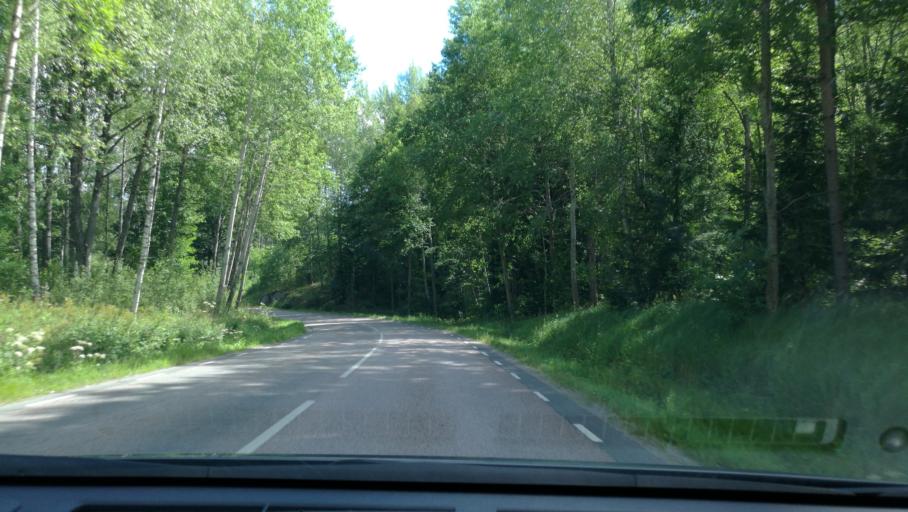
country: SE
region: OEstergoetland
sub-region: Norrkopings Kommun
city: Krokek
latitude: 58.6693
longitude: 16.4319
